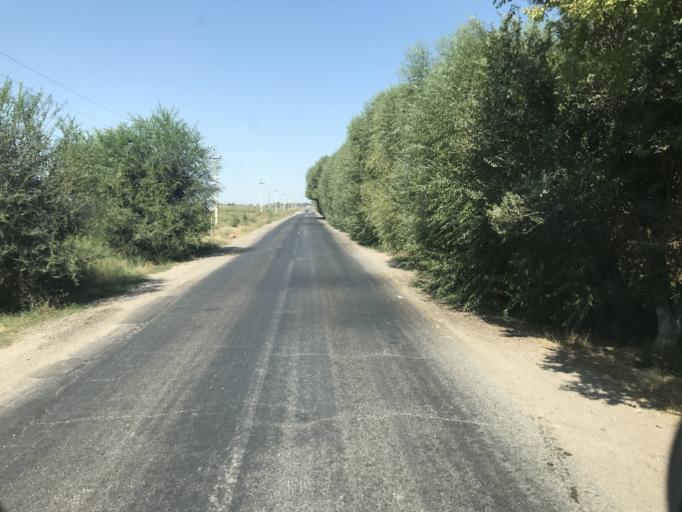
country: KZ
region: Ongtustik Qazaqstan
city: Ilyich
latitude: 40.9492
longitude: 68.4876
